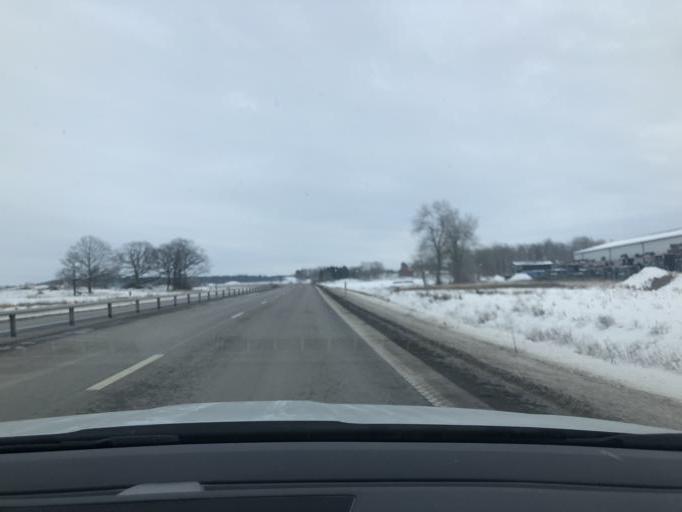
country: SE
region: OEstergoetland
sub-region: Linkopings Kommun
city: Sturefors
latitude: 58.3993
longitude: 15.7010
